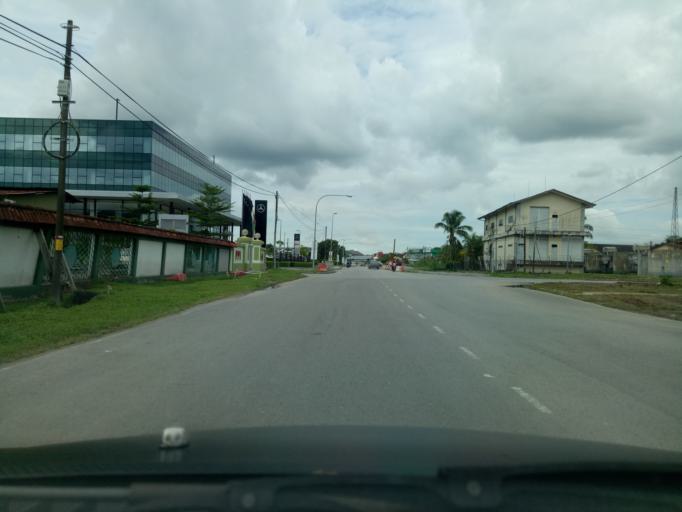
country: MY
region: Sarawak
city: Kuching
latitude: 1.5526
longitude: 110.3747
